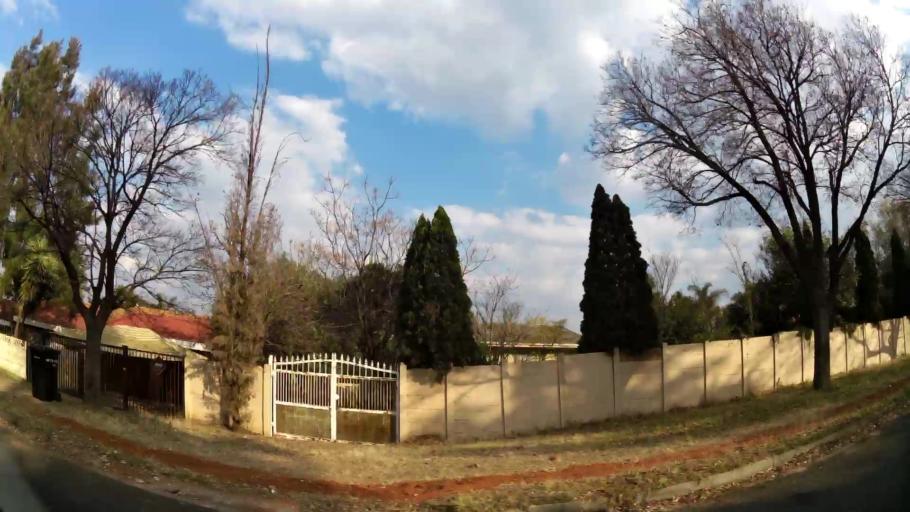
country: ZA
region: Gauteng
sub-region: Ekurhuleni Metropolitan Municipality
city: Germiston
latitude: -26.2457
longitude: 28.1775
